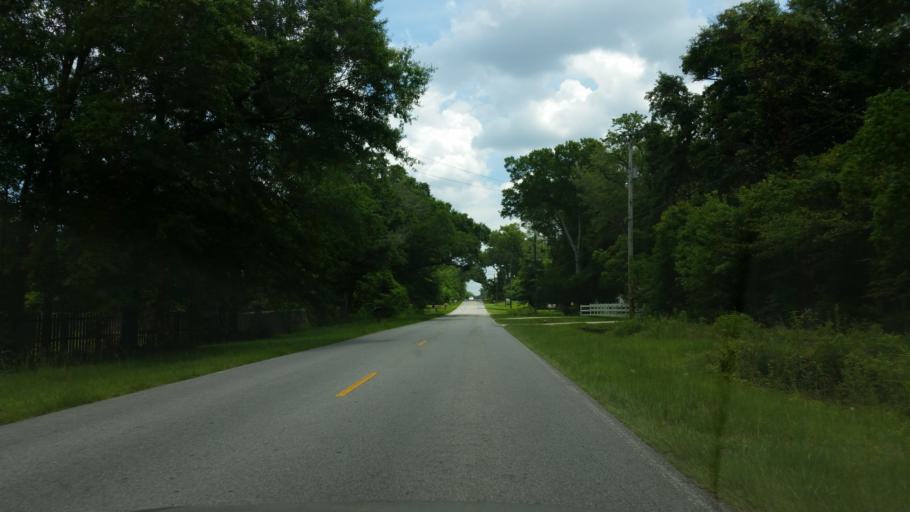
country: US
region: Florida
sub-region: Escambia County
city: Ensley
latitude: 30.5482
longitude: -87.2888
